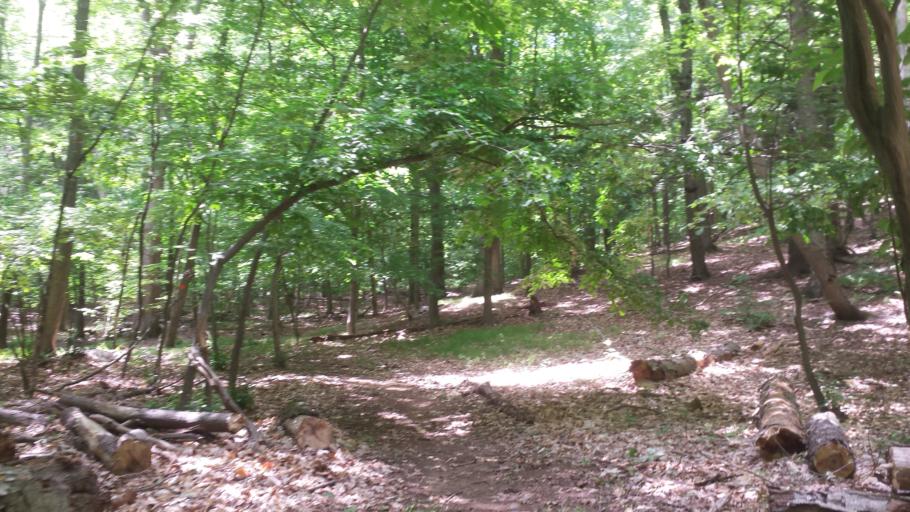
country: US
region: New York
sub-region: Putnam County
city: Peach Lake
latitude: 41.3083
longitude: -73.5715
